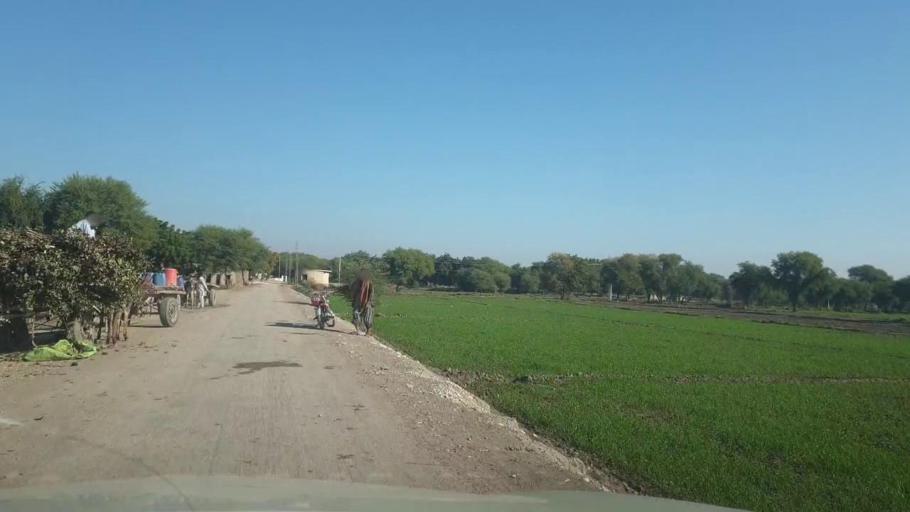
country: PK
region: Sindh
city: Bhan
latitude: 26.5432
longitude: 67.6734
